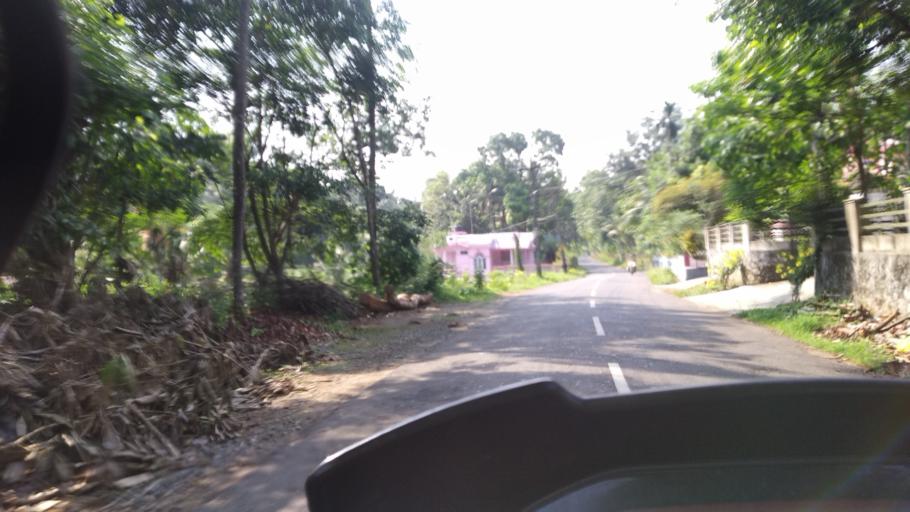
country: IN
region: Kerala
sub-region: Kottayam
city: Palackattumala
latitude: 9.7989
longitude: 76.5861
